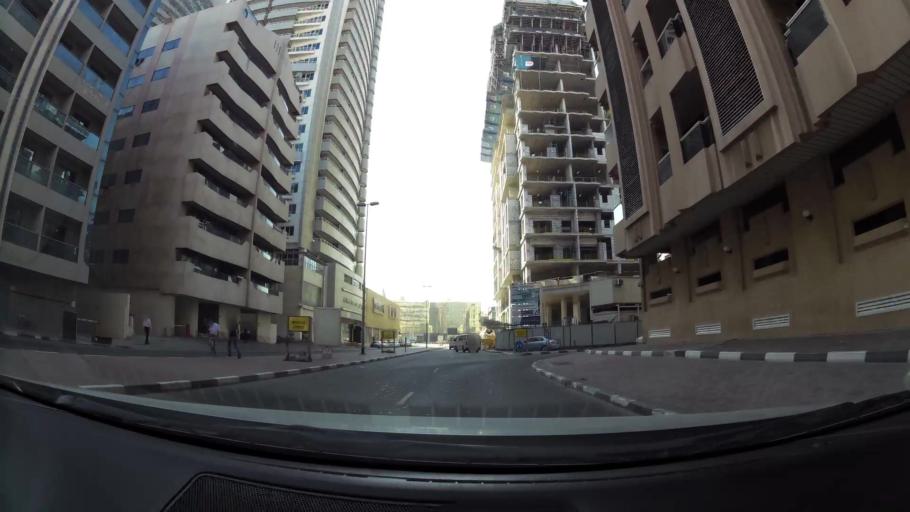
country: AE
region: Ash Shariqah
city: Sharjah
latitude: 25.2512
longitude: 55.2995
